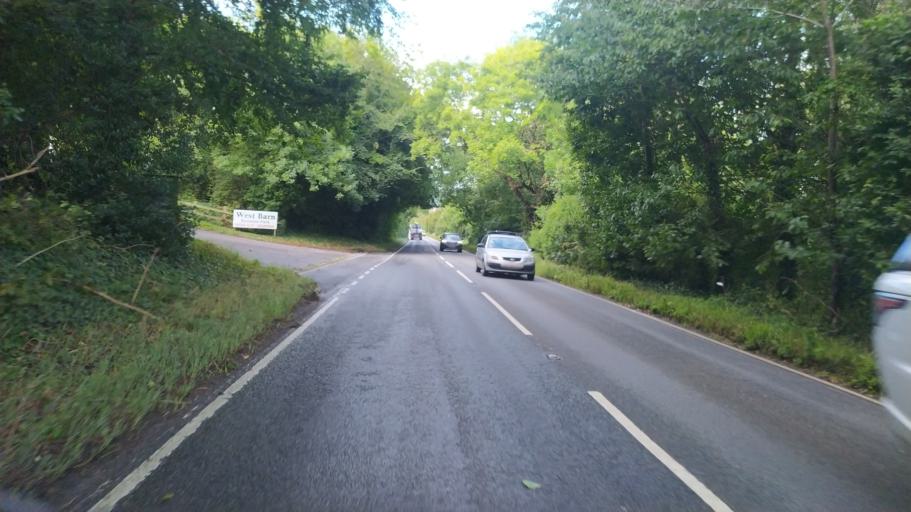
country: GB
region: England
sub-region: Dorset
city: Blandford Forum
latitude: 50.8587
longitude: -2.1374
